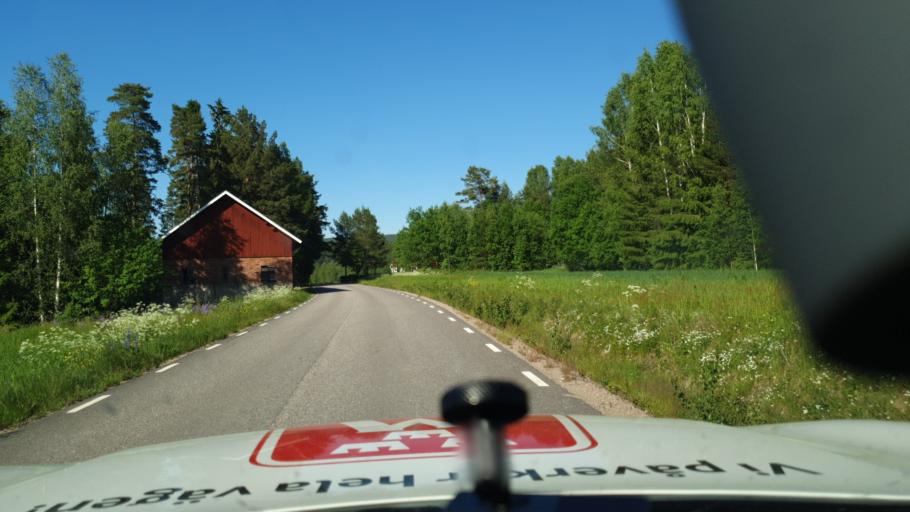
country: SE
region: Vaermland
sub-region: Torsby Kommun
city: Torsby
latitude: 60.1816
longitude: 13.0364
